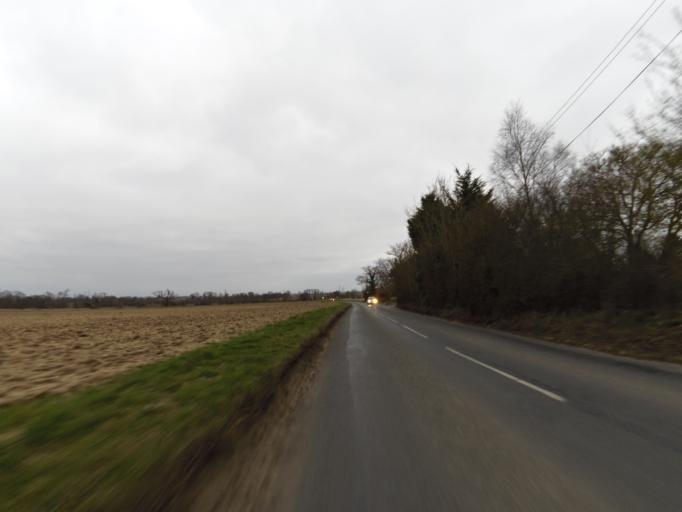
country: GB
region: England
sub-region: Suffolk
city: Ipswich
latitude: 52.1147
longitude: 1.1511
